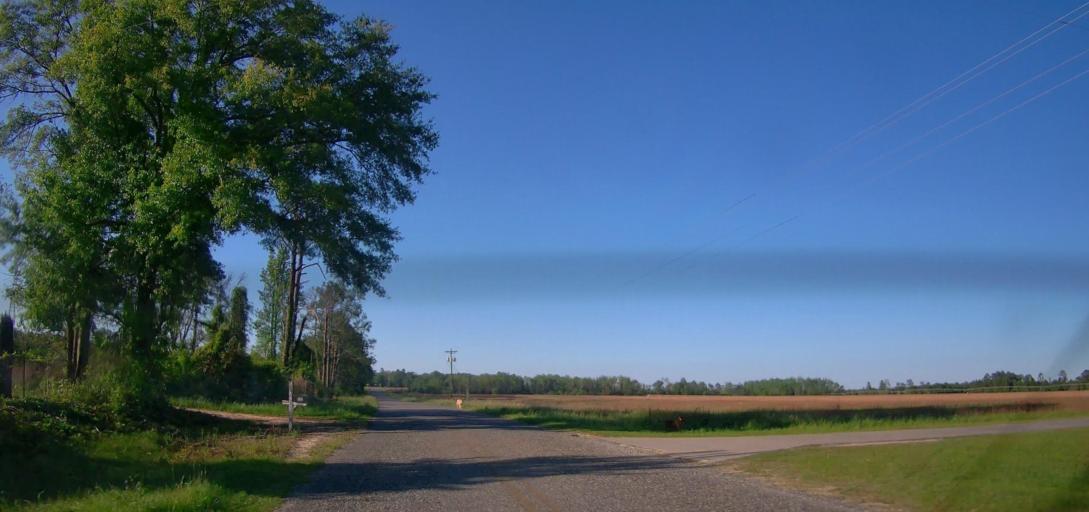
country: US
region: Georgia
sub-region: Ben Hill County
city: Fitzgerald
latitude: 31.6971
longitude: -83.1532
